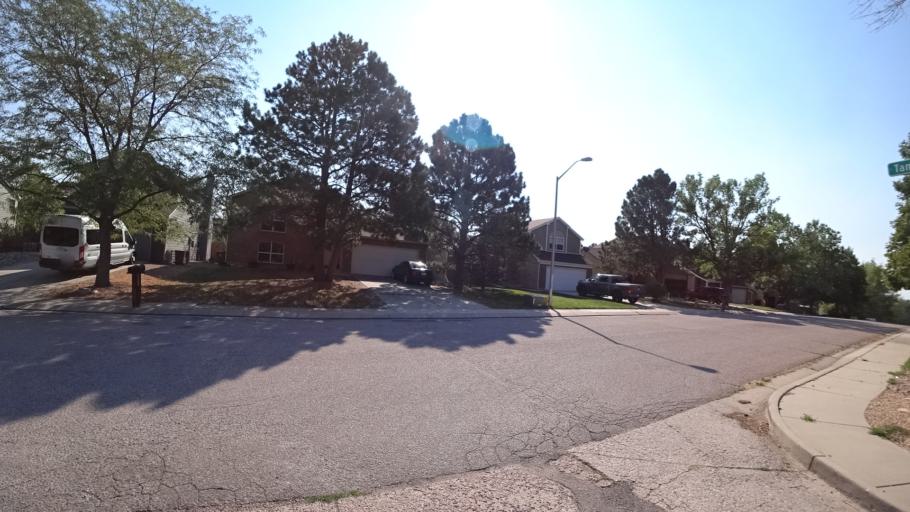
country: US
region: Colorado
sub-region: El Paso County
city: Stratmoor
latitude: 38.7810
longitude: -104.8006
